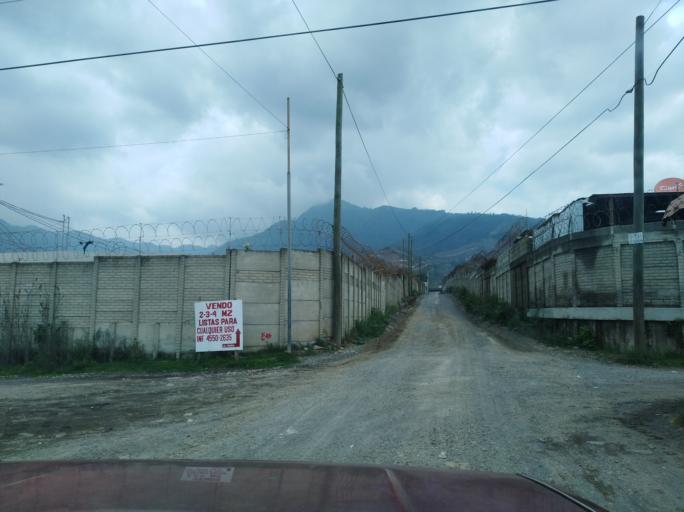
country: GT
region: Guatemala
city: Amatitlan
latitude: 14.5239
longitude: -90.6253
